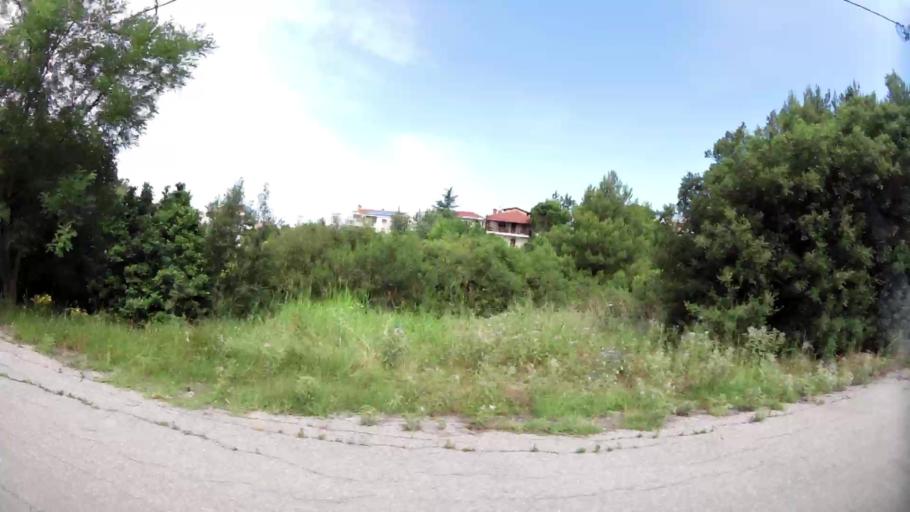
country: GR
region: Central Macedonia
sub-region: Nomos Thessalonikis
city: Panorama
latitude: 40.5764
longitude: 23.0112
